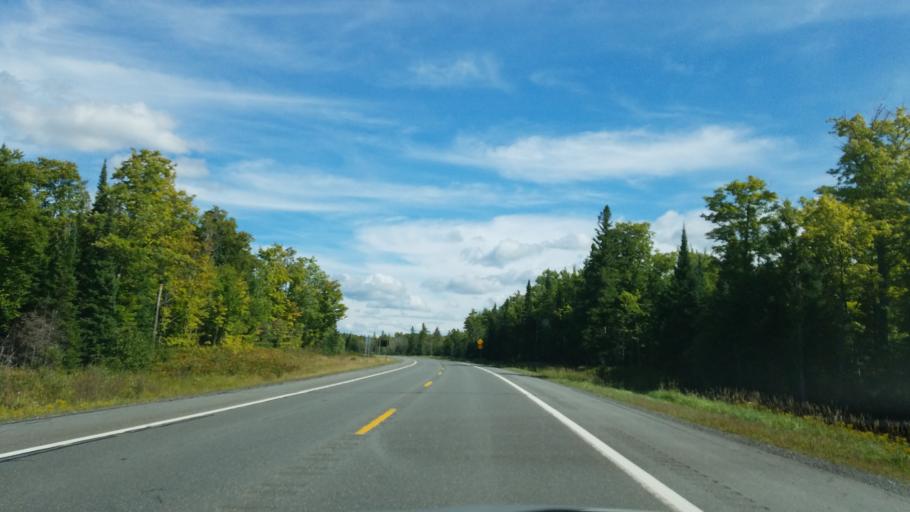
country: US
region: Michigan
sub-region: Baraga County
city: L'Anse
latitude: 46.5833
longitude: -88.4695
